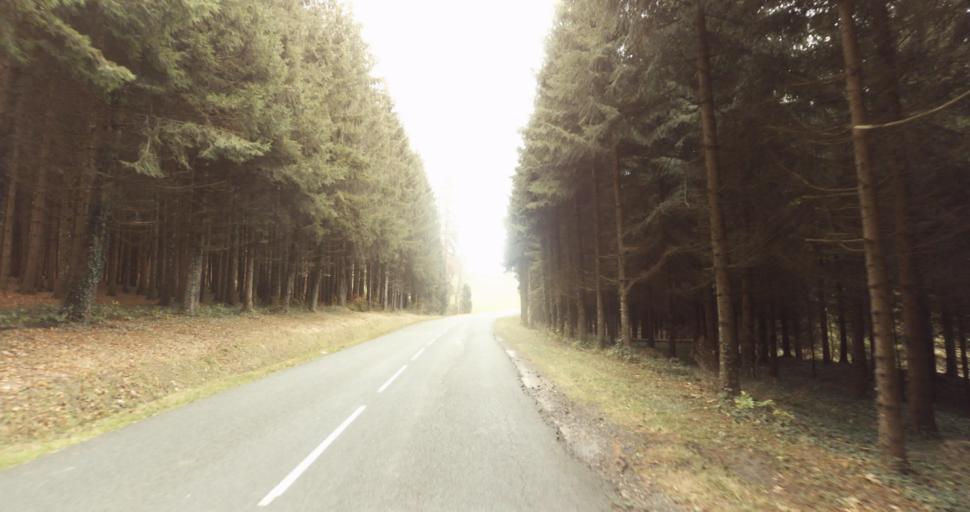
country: FR
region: Rhone-Alpes
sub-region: Departement de la Haute-Savoie
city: Evires
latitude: 46.0413
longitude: 6.2162
